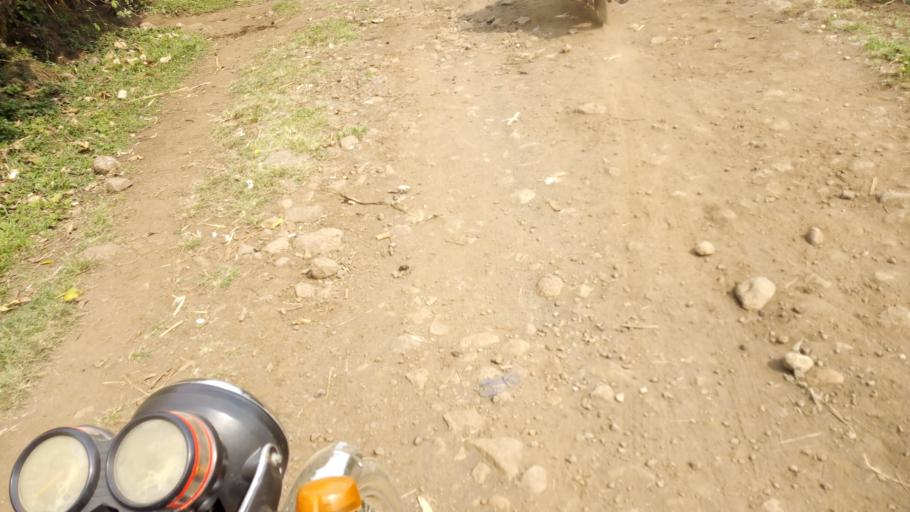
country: UG
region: Western Region
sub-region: Kisoro District
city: Kisoro
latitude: -1.3329
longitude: 29.6143
